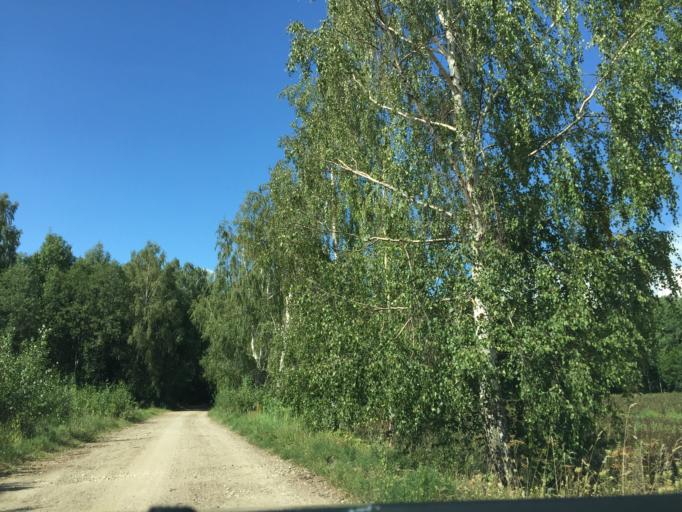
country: LT
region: Siauliu apskritis
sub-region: Joniskis
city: Joniskis
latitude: 56.3338
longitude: 23.5606
